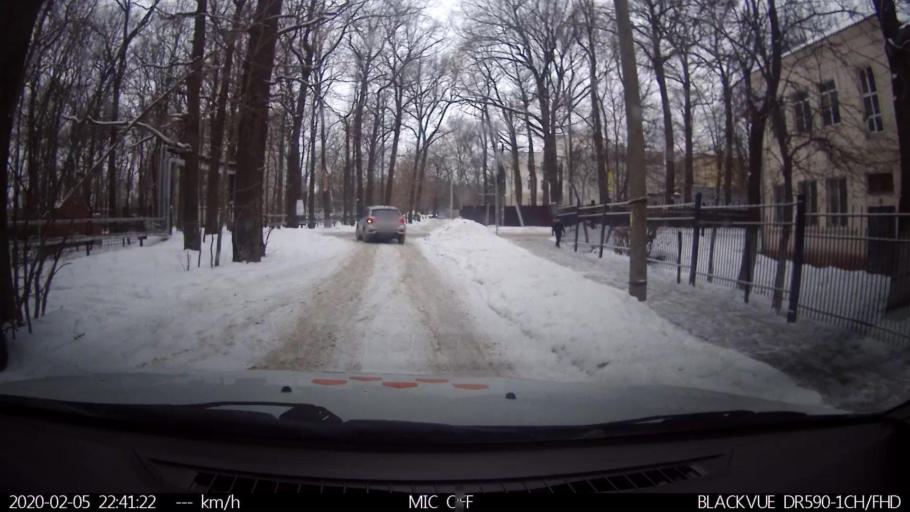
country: RU
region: Nizjnij Novgorod
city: Imeni Stepana Razina
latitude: 54.7210
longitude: 44.3371
